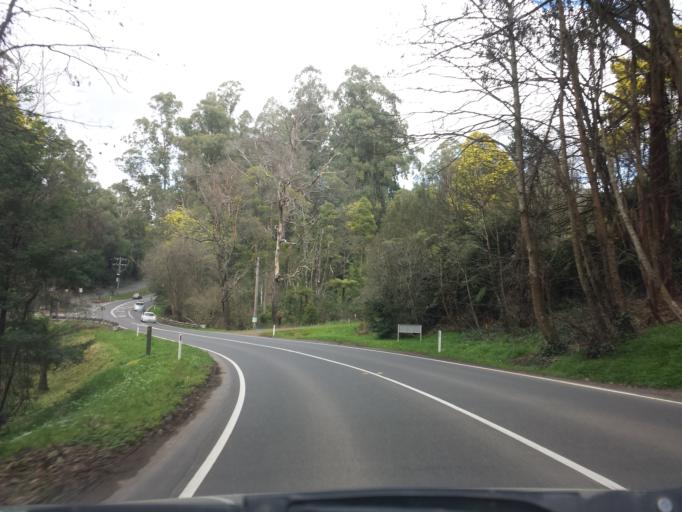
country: AU
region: Victoria
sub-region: Yarra Ranges
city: Monbulk
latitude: -37.8782
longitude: 145.3964
